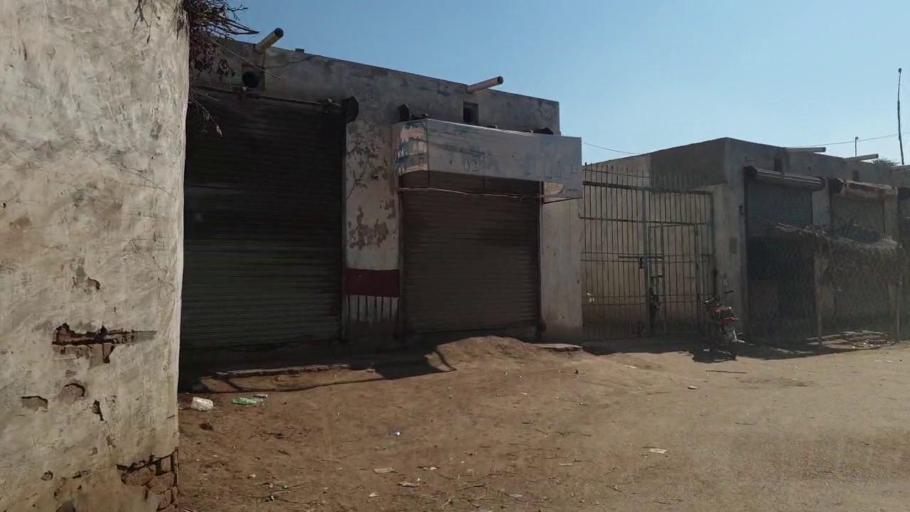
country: PK
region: Sindh
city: Shahpur Chakar
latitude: 26.1047
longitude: 68.6358
